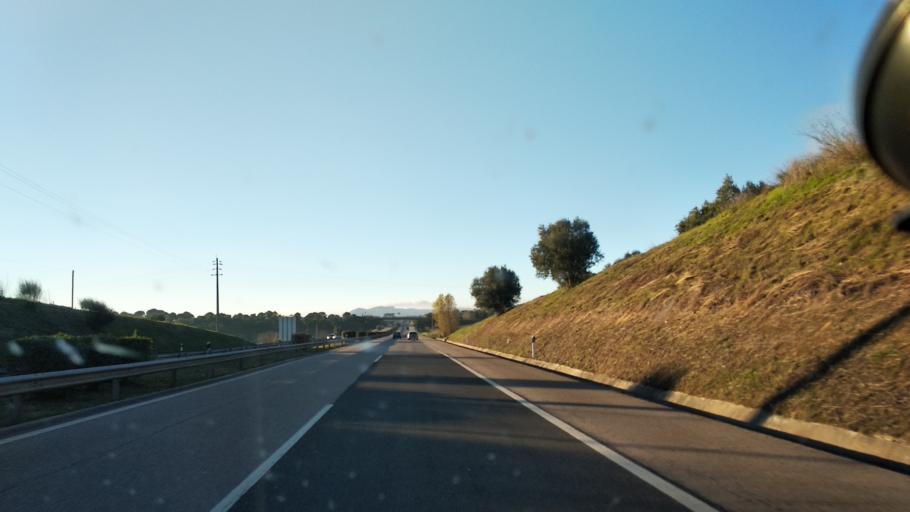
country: PT
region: Santarem
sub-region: Torres Novas
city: Torres Novas
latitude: 39.4657
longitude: -8.5567
